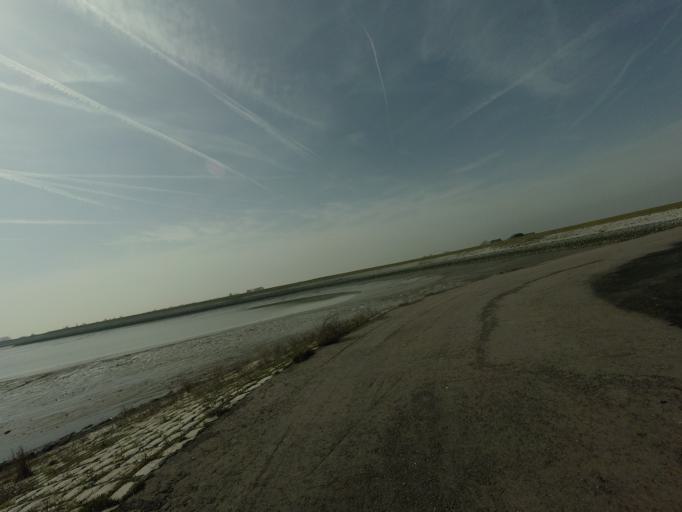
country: NL
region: Zeeland
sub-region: Gemeente Reimerswaal
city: Yerseke
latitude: 51.3966
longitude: 4.0229
